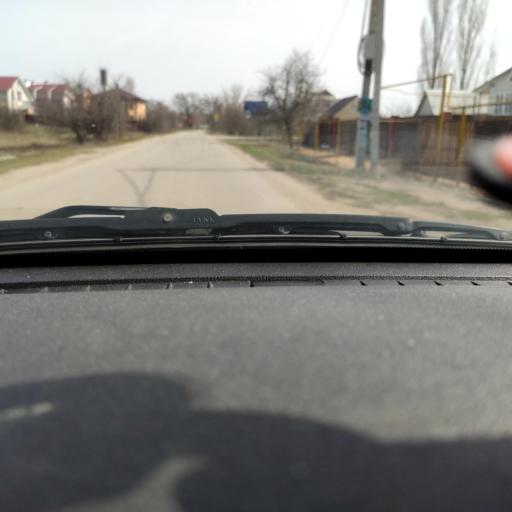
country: RU
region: Voronezj
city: Novaya Usman'
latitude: 51.6274
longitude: 39.4130
